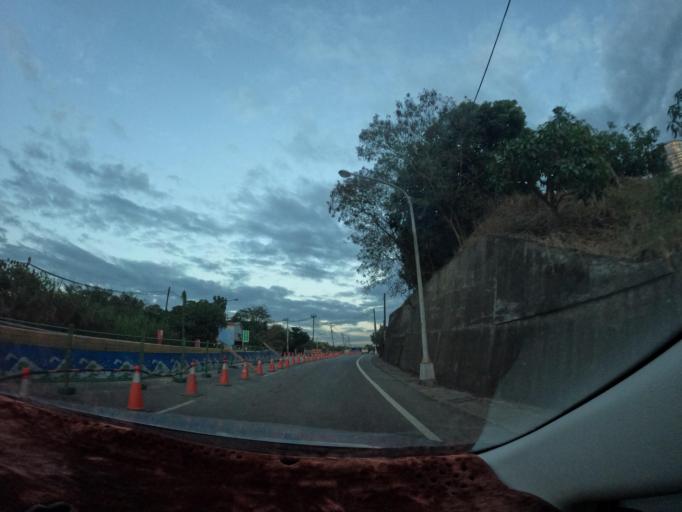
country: TW
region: Taiwan
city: Yujing
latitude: 23.0882
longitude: 120.4299
